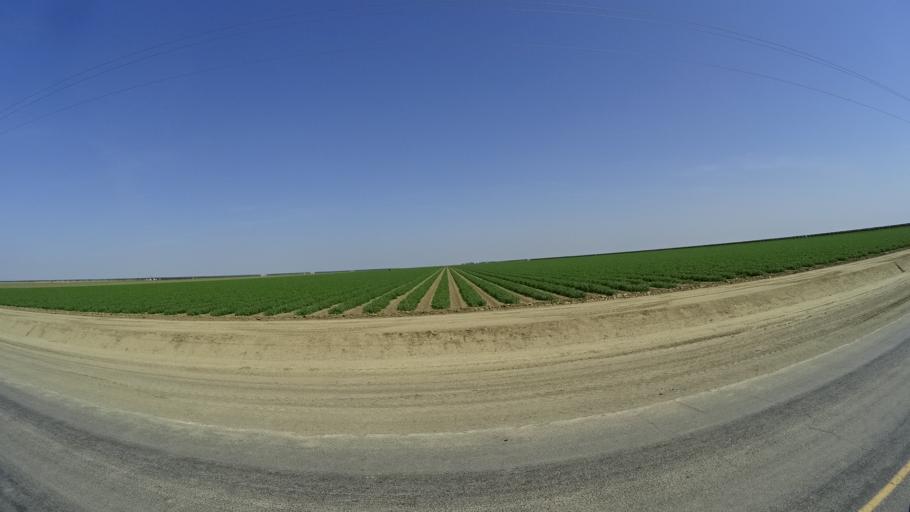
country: US
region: California
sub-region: Kings County
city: Kettleman City
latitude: 36.1377
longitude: -119.9625
